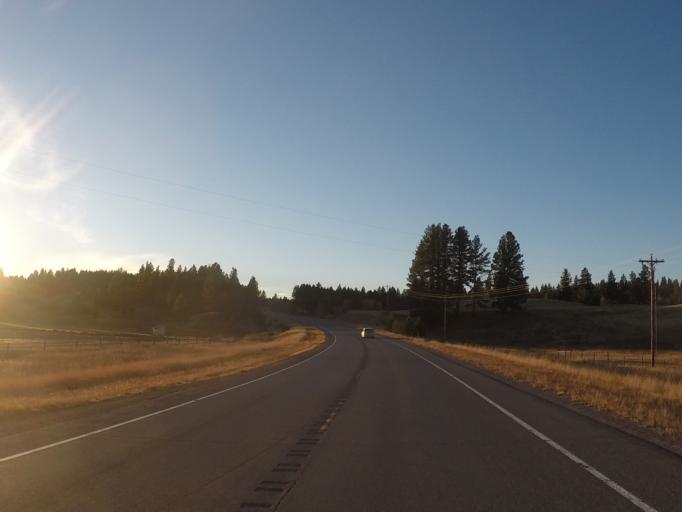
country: US
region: Montana
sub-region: Lewis and Clark County
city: Lincoln
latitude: 47.0070
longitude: -113.0497
